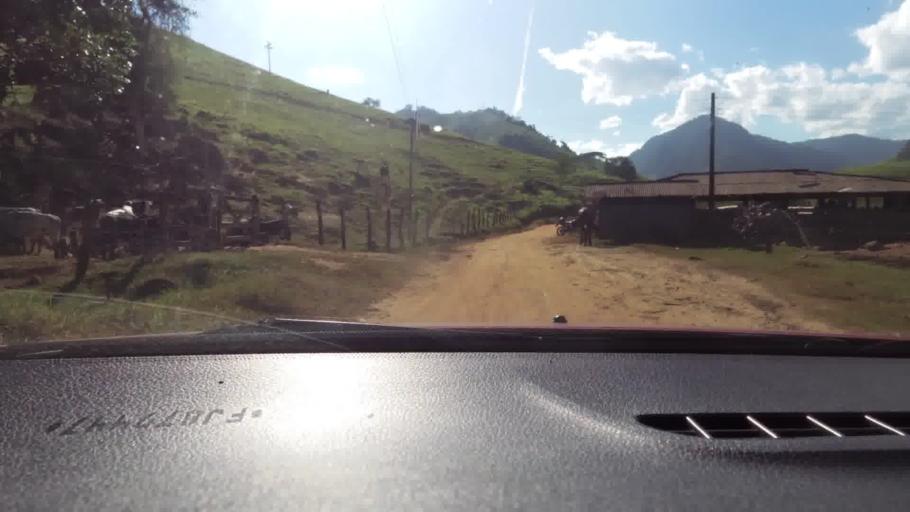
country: BR
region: Espirito Santo
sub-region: Guarapari
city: Guarapari
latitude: -20.5329
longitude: -40.5626
